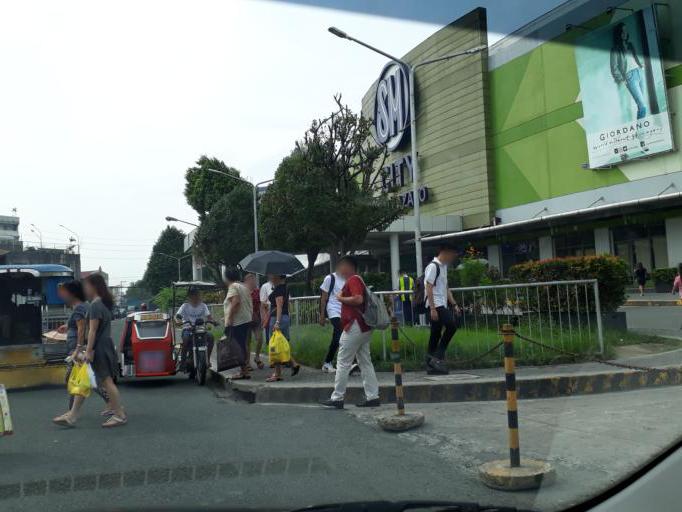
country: PH
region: Metro Manila
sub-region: City of Manila
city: Manila
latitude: 14.6173
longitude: 120.9856
